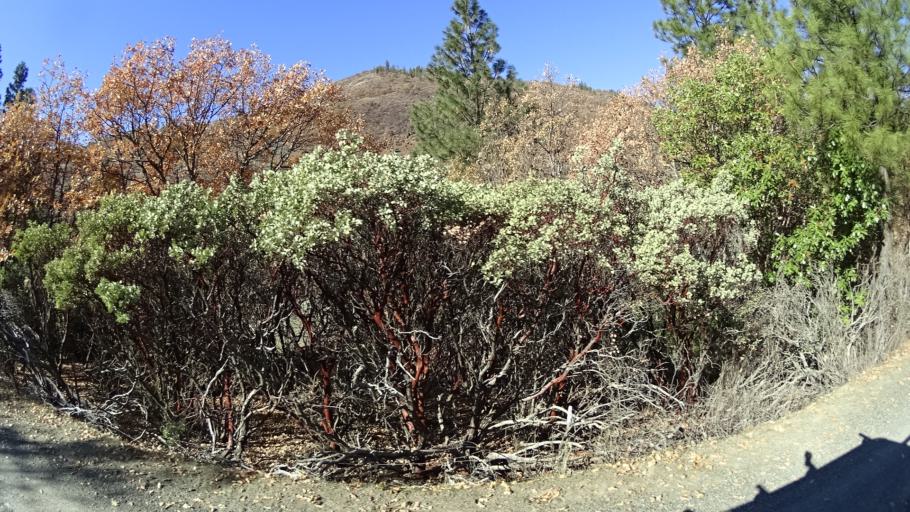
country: US
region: California
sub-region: Siskiyou County
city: Yreka
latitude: 41.8455
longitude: -122.8368
